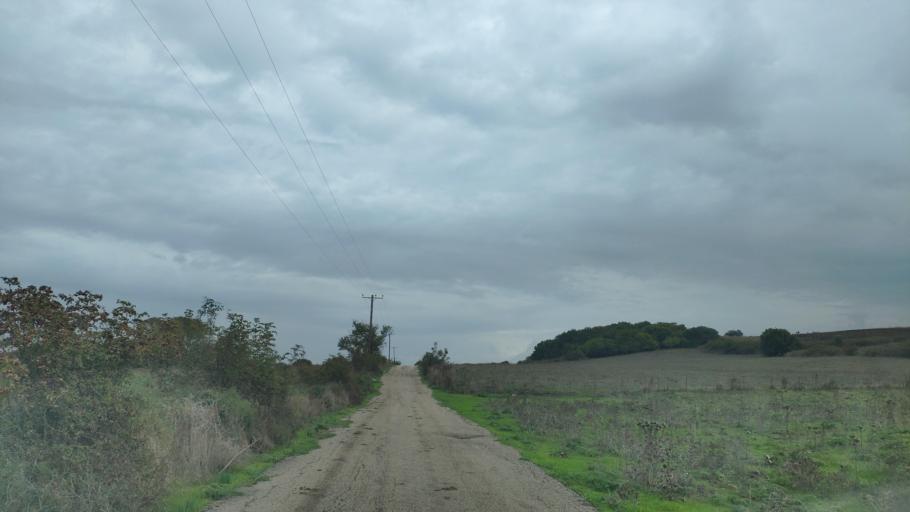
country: GR
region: West Greece
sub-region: Nomos Aitolias kai Akarnanias
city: Monastirakion
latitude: 38.9208
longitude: 21.0118
